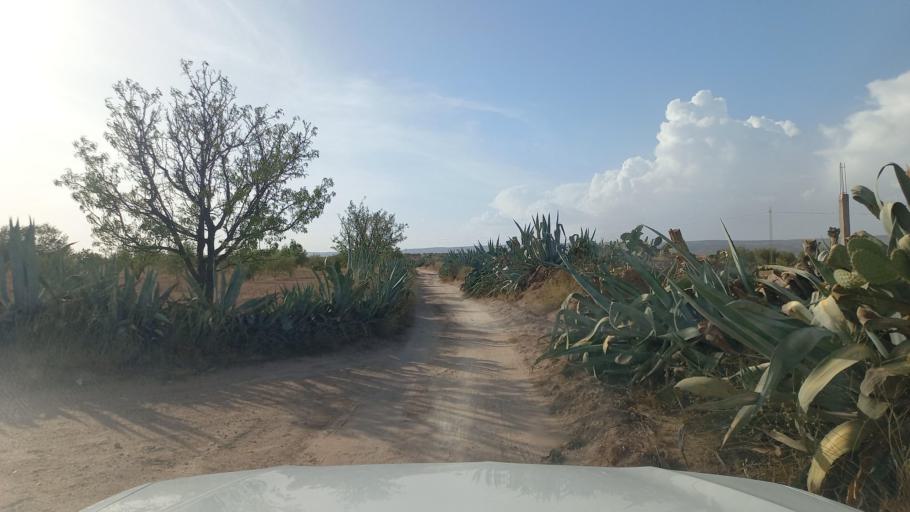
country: TN
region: Al Qasrayn
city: Kasserine
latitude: 35.2313
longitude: 8.9239
